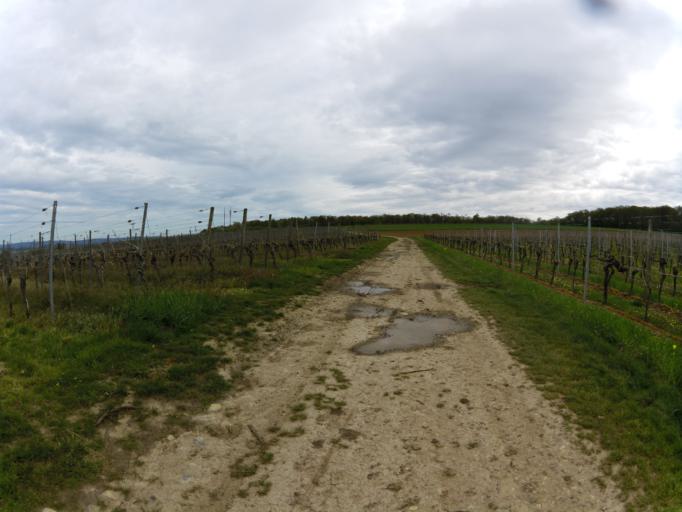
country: DE
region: Bavaria
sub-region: Regierungsbezirk Unterfranken
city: Prosselsheim
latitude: 49.8619
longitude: 10.1584
